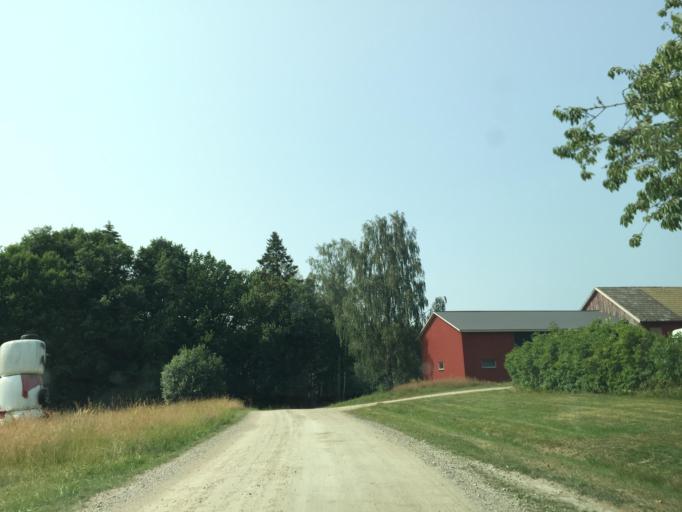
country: SE
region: Vaestra Goetaland
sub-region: Trollhattan
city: Sjuntorp
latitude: 58.2689
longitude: 12.1034
